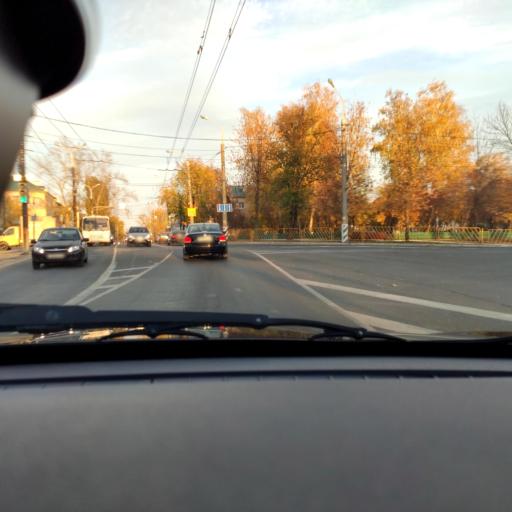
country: RU
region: Samara
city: Tol'yatti
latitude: 53.4781
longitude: 49.3654
